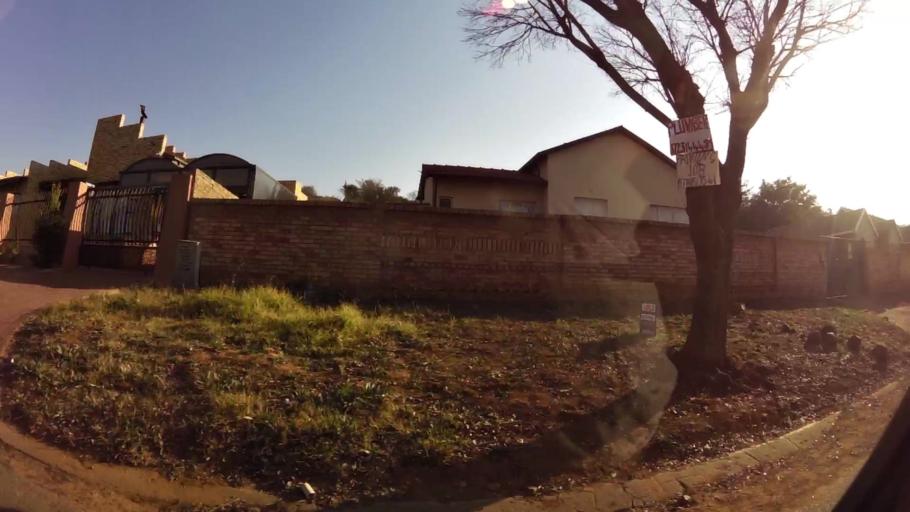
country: ZA
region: Gauteng
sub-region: City of Johannesburg Metropolitan Municipality
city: Soweto
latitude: -26.2936
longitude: 27.9570
